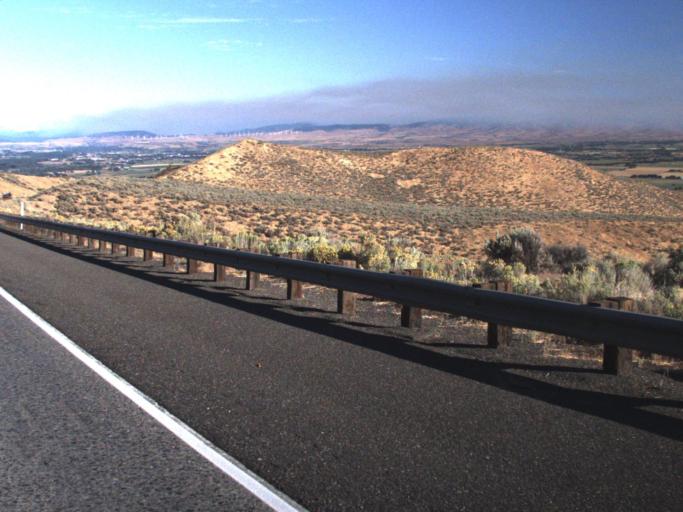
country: US
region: Washington
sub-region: Kittitas County
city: Kittitas
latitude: 46.8944
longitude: -120.4440
